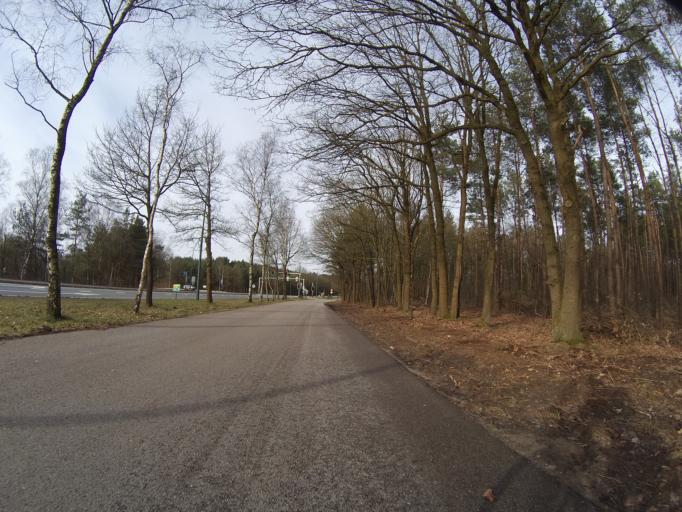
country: NL
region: Utrecht
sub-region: Gemeente Amersfoort
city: Amersfoort
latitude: 52.1201
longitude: 5.3628
